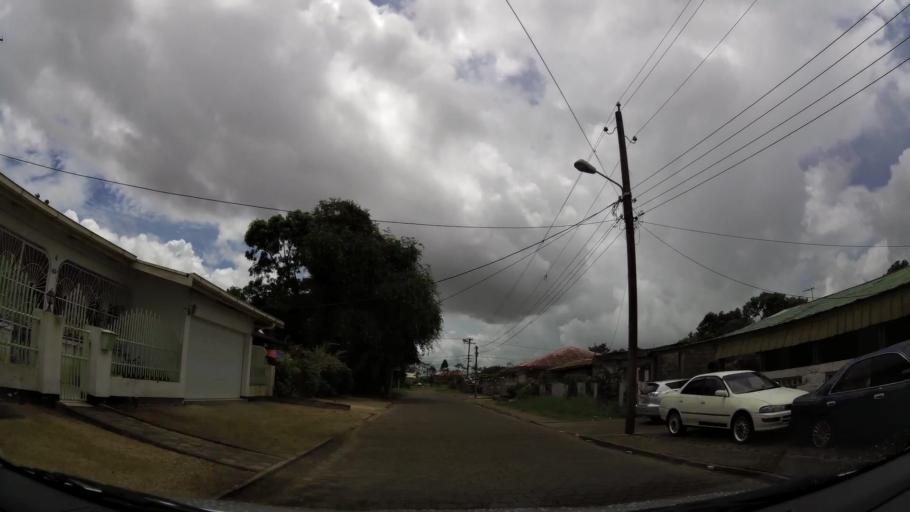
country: SR
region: Paramaribo
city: Paramaribo
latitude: 5.8271
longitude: -55.2240
